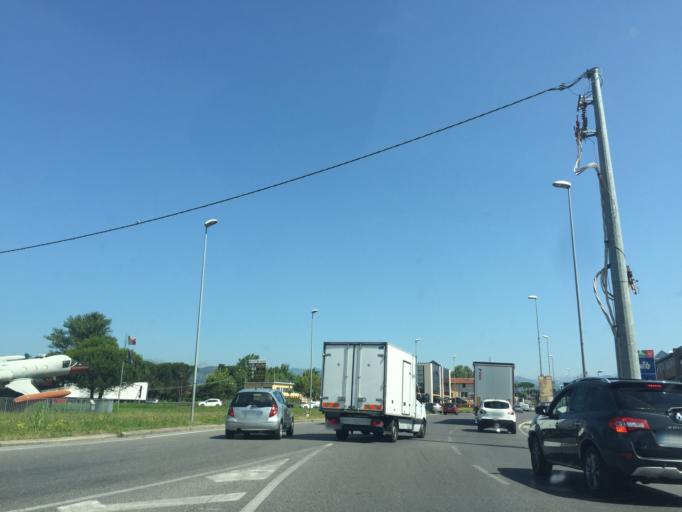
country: IT
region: Tuscany
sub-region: Provincia di Lucca
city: Lucca
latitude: 43.8312
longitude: 10.4942
